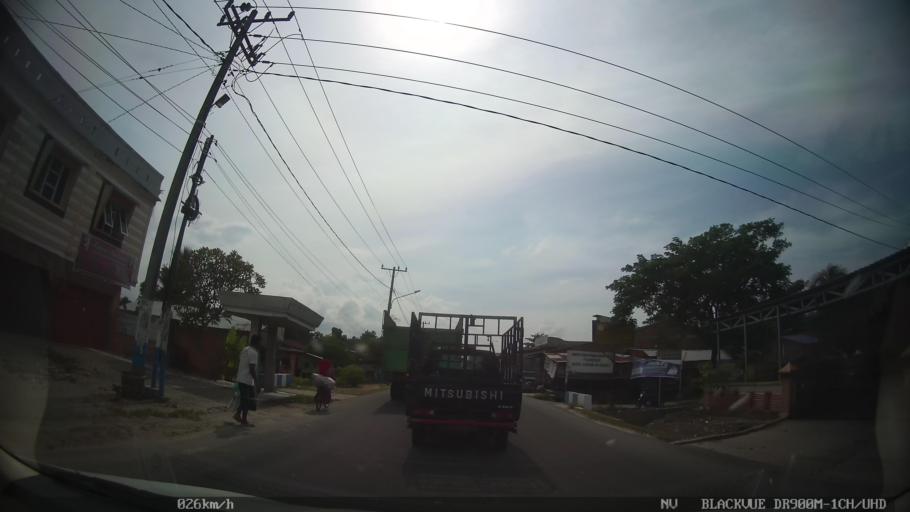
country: ID
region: North Sumatra
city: Percut
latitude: 3.6112
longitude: 98.8274
